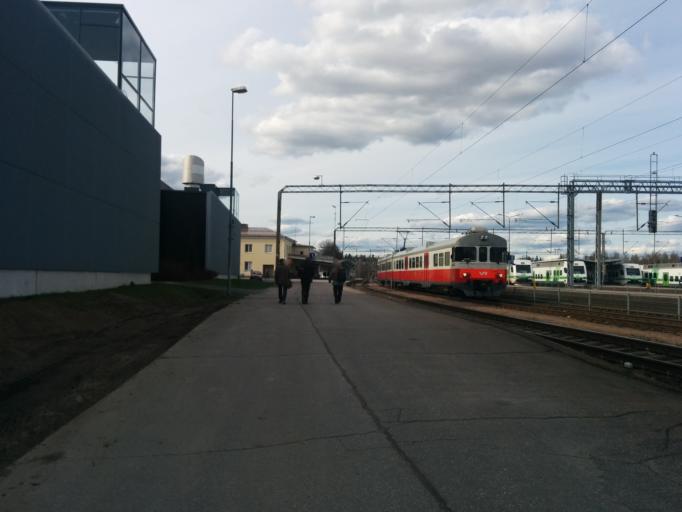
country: FI
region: Haeme
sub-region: Riihimaeki
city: Riihimaeki
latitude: 60.7338
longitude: 24.7820
